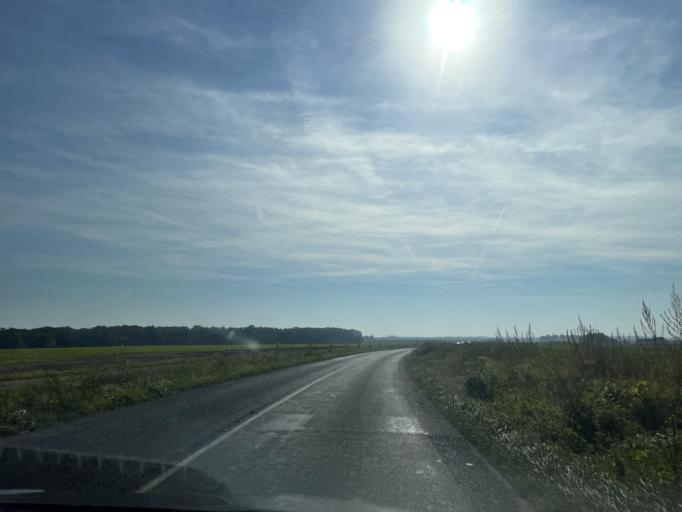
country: FR
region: Ile-de-France
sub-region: Departement de Seine-et-Marne
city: Sammeron
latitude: 48.8925
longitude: 3.0651
